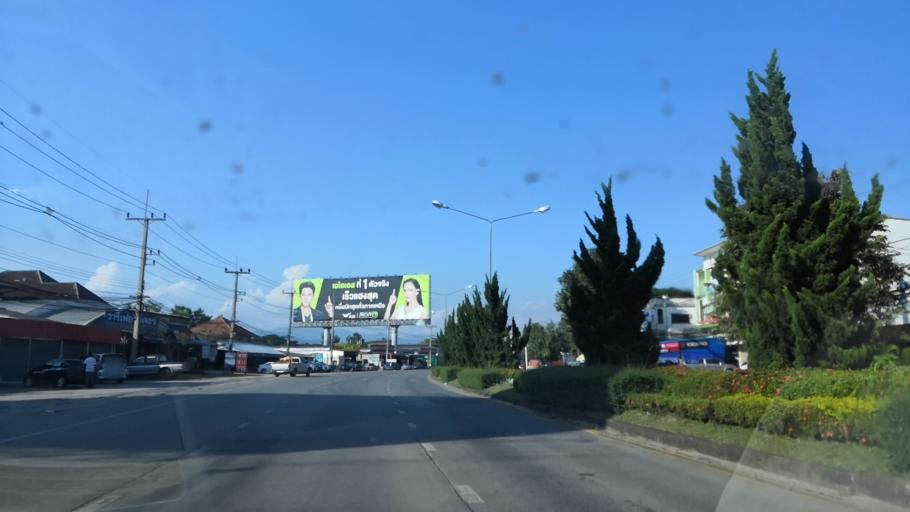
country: TH
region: Chiang Rai
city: Chiang Rai
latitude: 19.9251
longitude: 99.8444
